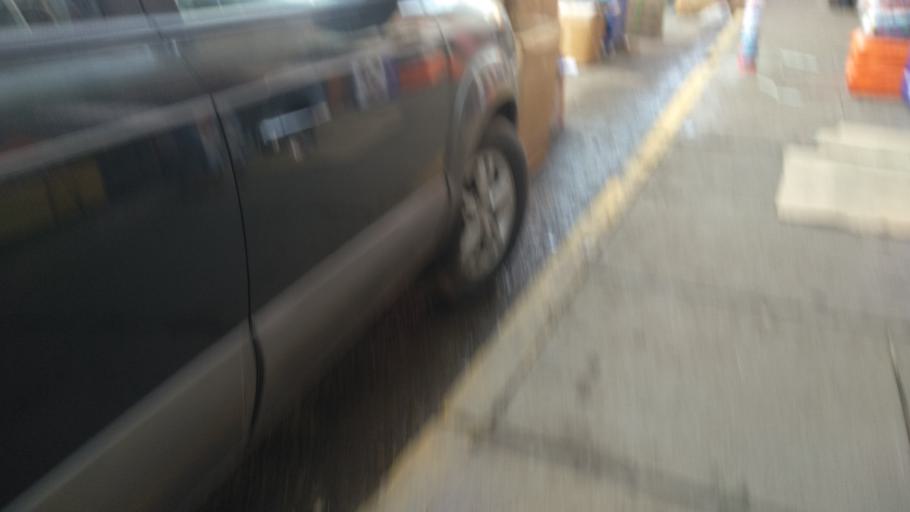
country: PE
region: Cusco
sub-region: Provincia de Cusco
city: Cusco
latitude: -13.5237
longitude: -71.9817
